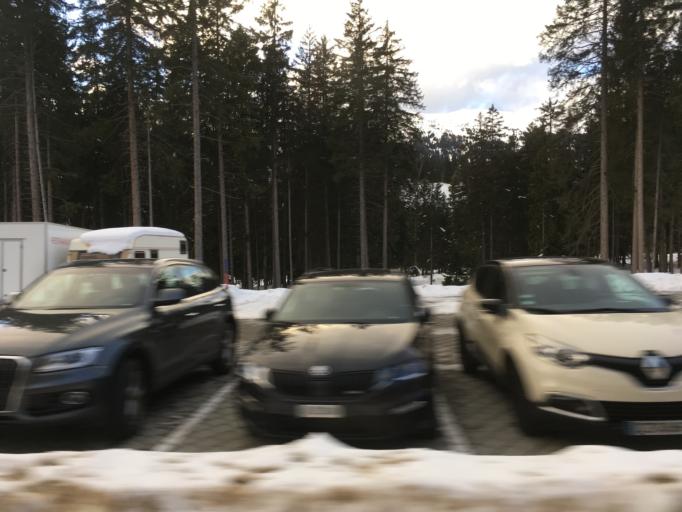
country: CH
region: Grisons
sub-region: Plessur District
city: Churwalden
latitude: 46.7223
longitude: 9.5587
